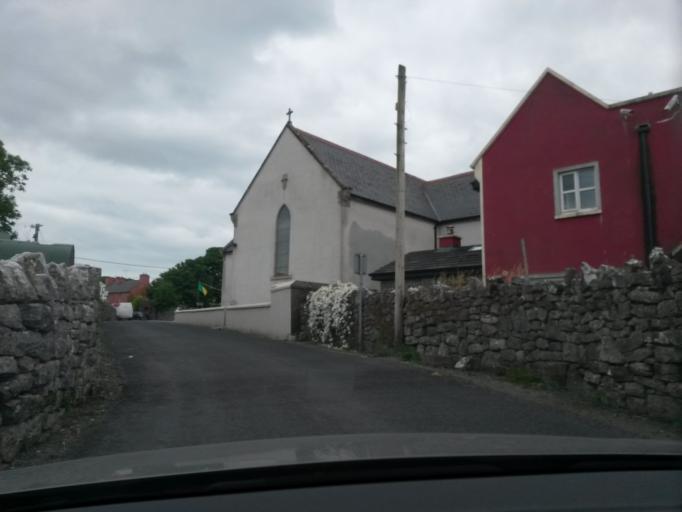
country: IE
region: Connaught
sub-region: County Galway
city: Bearna
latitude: 52.9903
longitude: -9.2195
